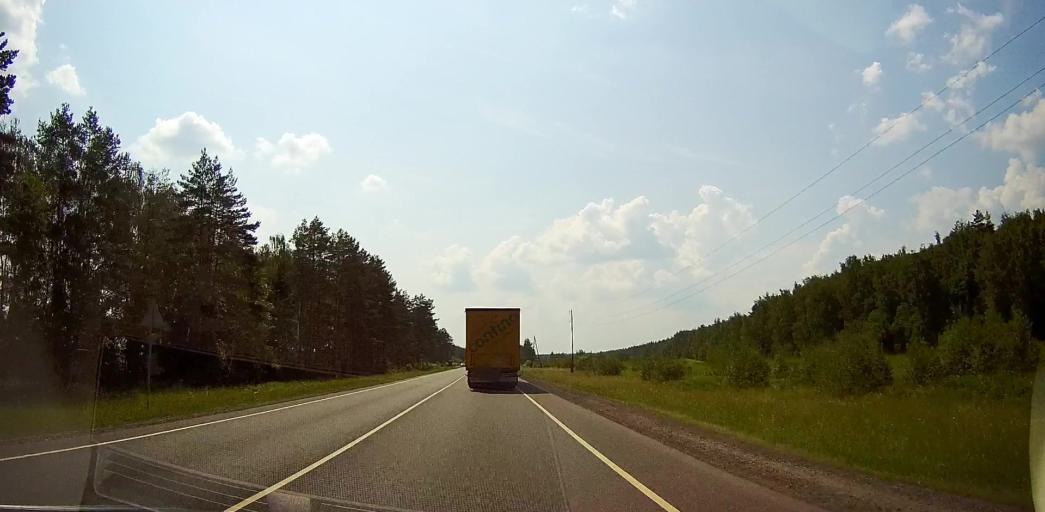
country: RU
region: Moskovskaya
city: Meshcherino
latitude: 55.1767
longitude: 38.3367
